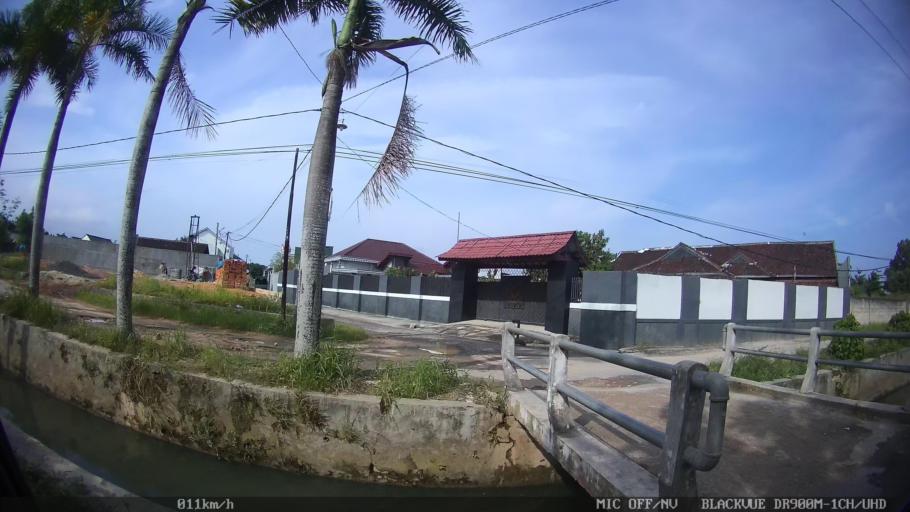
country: ID
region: Lampung
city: Kedaton
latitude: -5.3757
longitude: 105.2966
